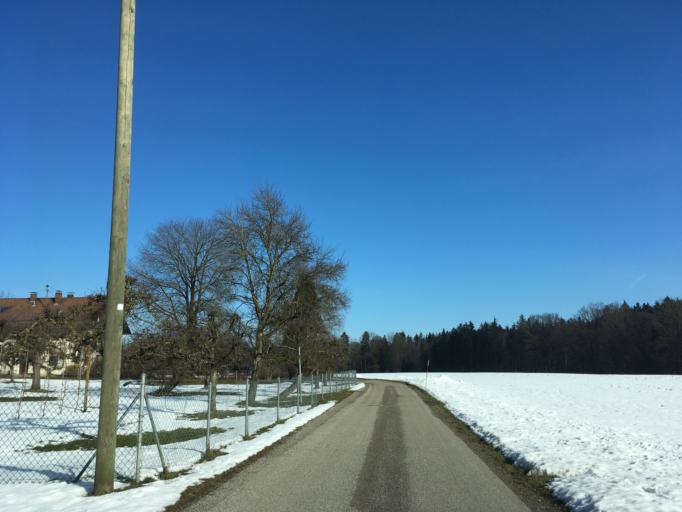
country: DE
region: Bavaria
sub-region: Upper Bavaria
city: Schechen
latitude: 47.9132
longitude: 12.1506
